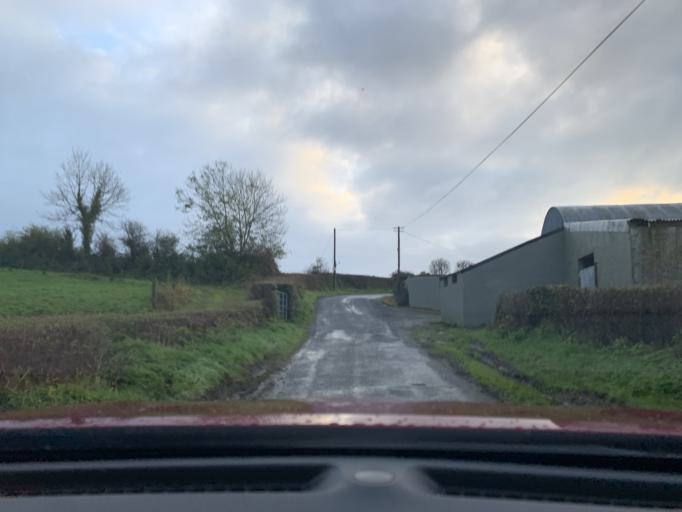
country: IE
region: Connaught
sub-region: Sligo
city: Ballymote
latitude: 54.0362
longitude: -8.5409
